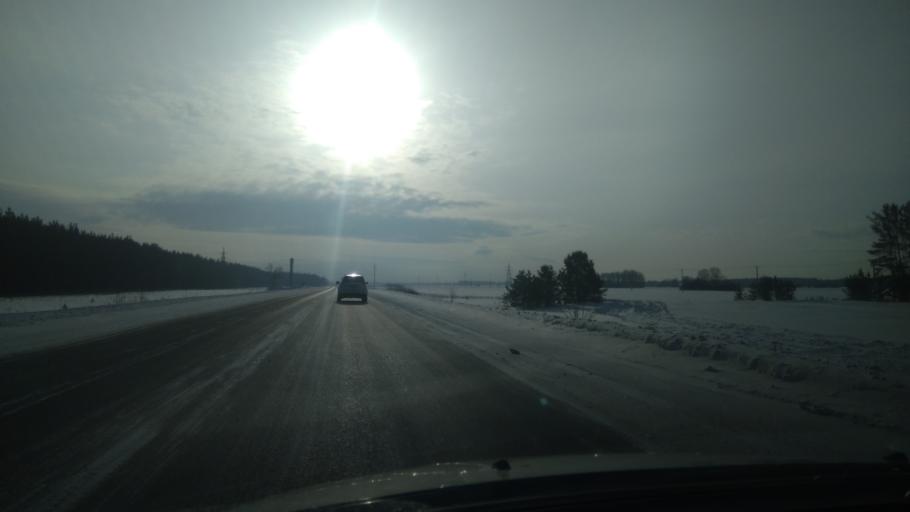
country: RU
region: Sverdlovsk
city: Sukhoy Log
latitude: 56.8690
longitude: 62.0467
